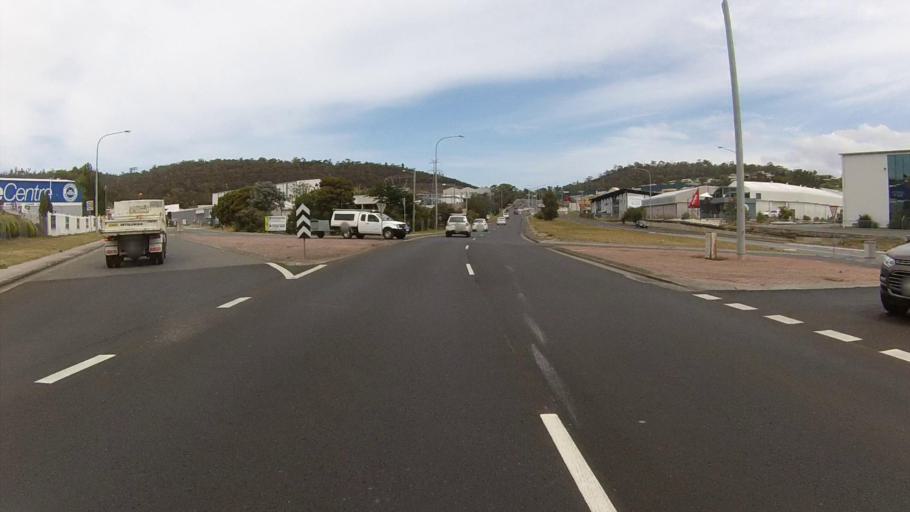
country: AU
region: Tasmania
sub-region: Clarence
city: Warrane
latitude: -42.8572
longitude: 147.3948
